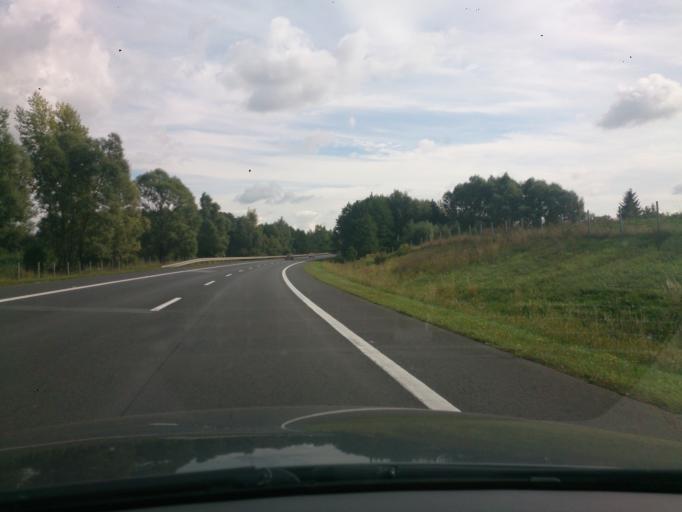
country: PL
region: Kujawsko-Pomorskie
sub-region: Powiat swiecki
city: Swiecie
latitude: 53.4213
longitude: 18.4373
